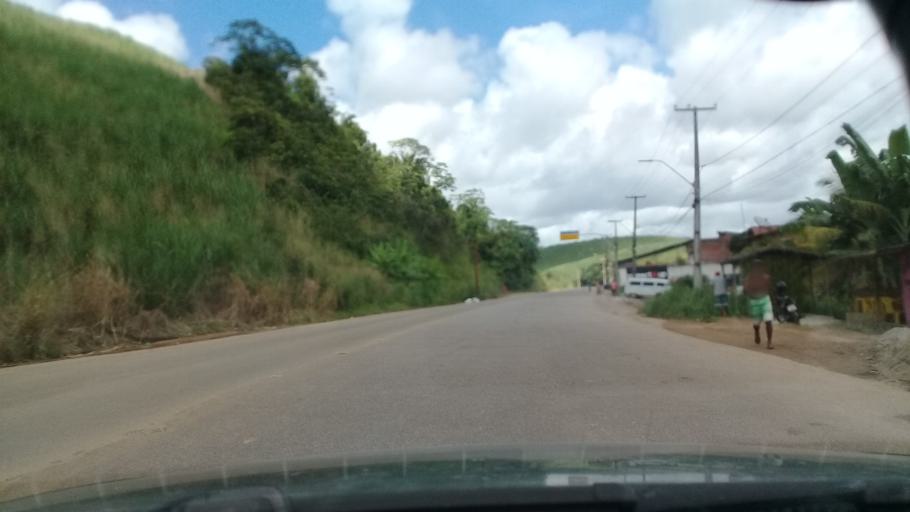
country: BR
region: Pernambuco
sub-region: Ipojuca
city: Ipojuca
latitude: -8.4196
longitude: -35.0724
